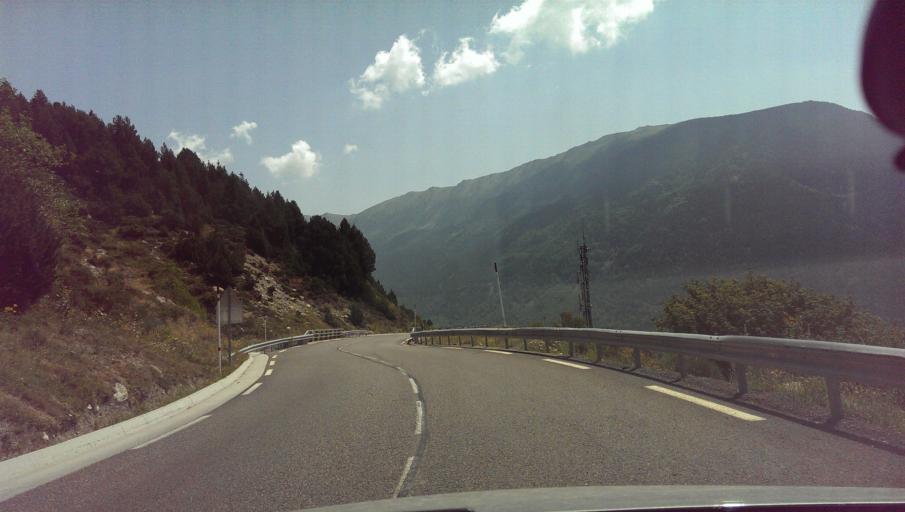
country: AD
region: Encamp
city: Pas de la Casa
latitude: 42.5519
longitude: 1.8232
